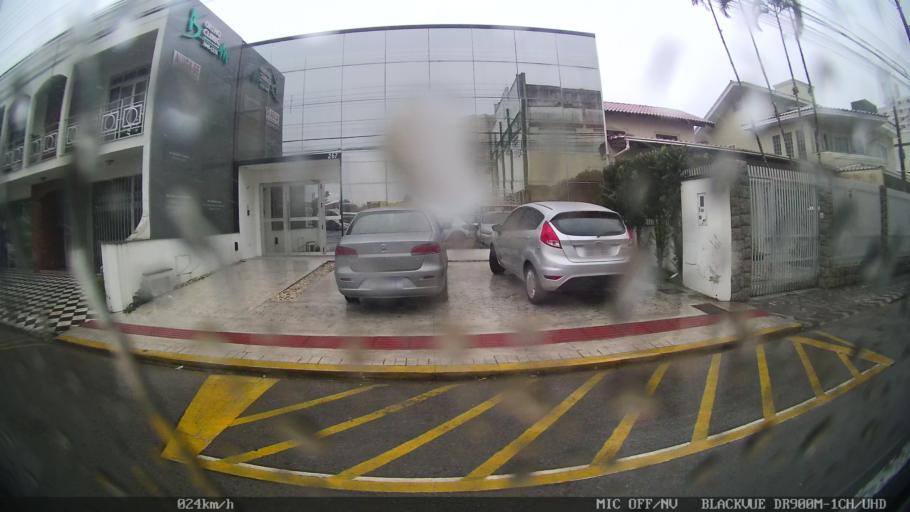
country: BR
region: Santa Catarina
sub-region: Itajai
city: Itajai
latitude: -26.9073
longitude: -48.6653
